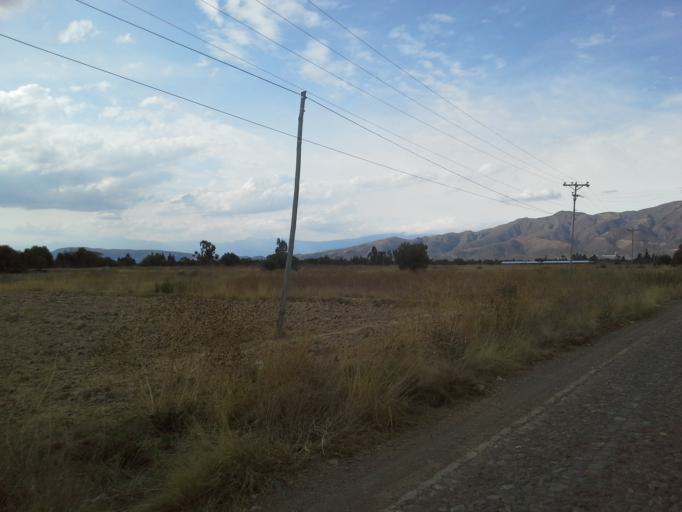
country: BO
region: Cochabamba
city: Tarata
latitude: -17.5978
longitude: -66.0187
